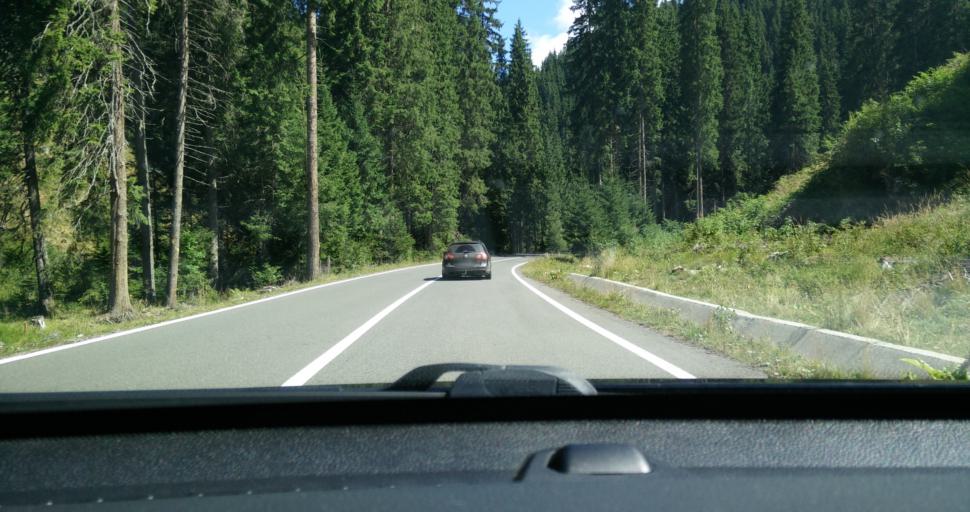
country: RO
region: Hunedoara
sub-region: Oras Petrila
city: Petrila
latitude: 45.5250
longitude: 23.6456
